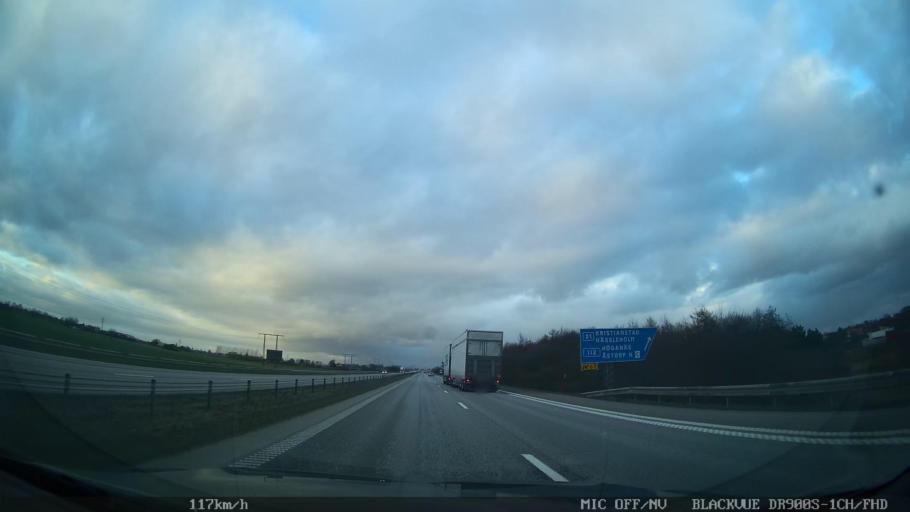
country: SE
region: Skane
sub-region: Astorps Kommun
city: Astorp
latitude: 56.1411
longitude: 12.9300
